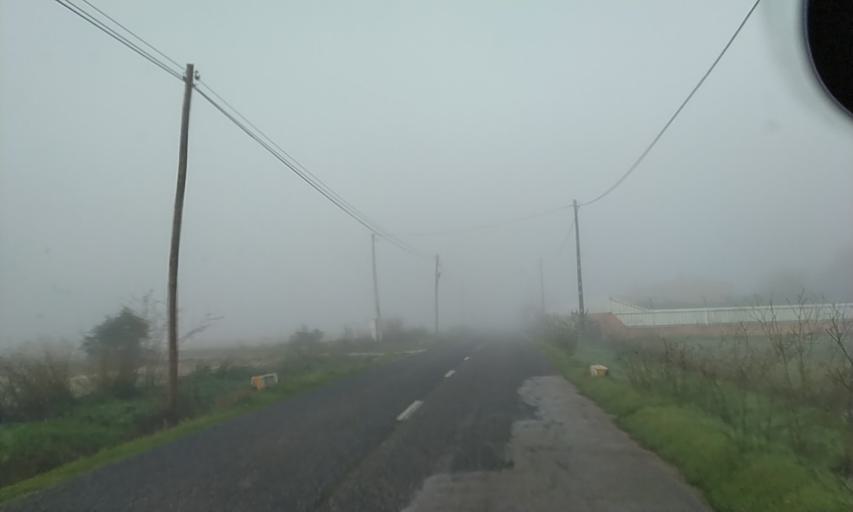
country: PT
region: Setubal
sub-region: Palmela
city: Palmela
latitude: 38.6073
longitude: -8.8533
